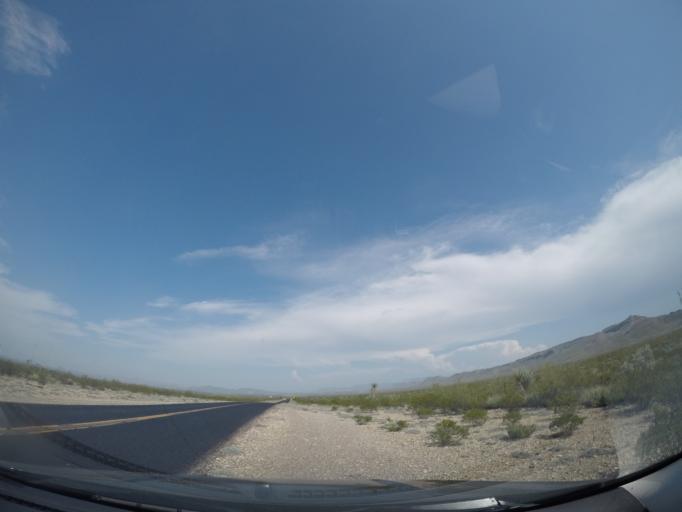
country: US
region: Texas
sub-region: Brewster County
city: Alpine
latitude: 29.6903
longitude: -103.1604
